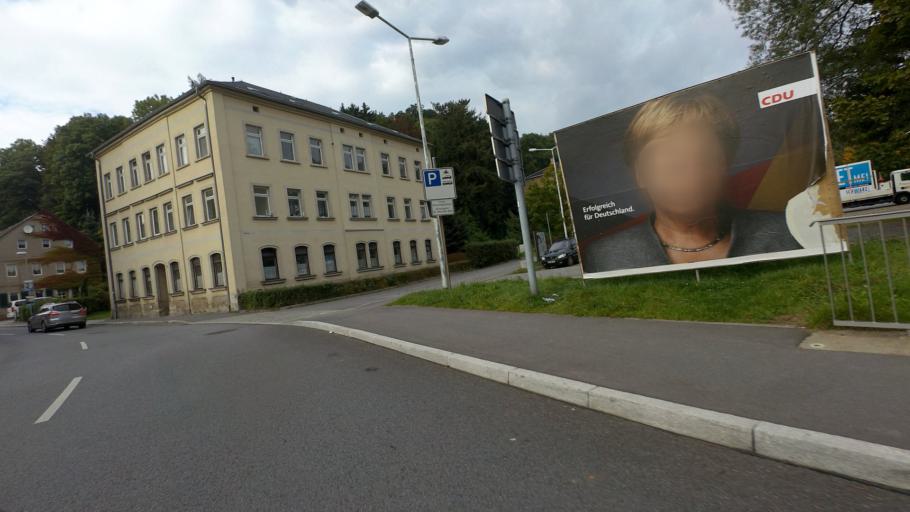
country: DE
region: Saxony
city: Sebnitz
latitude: 50.9760
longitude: 14.2820
